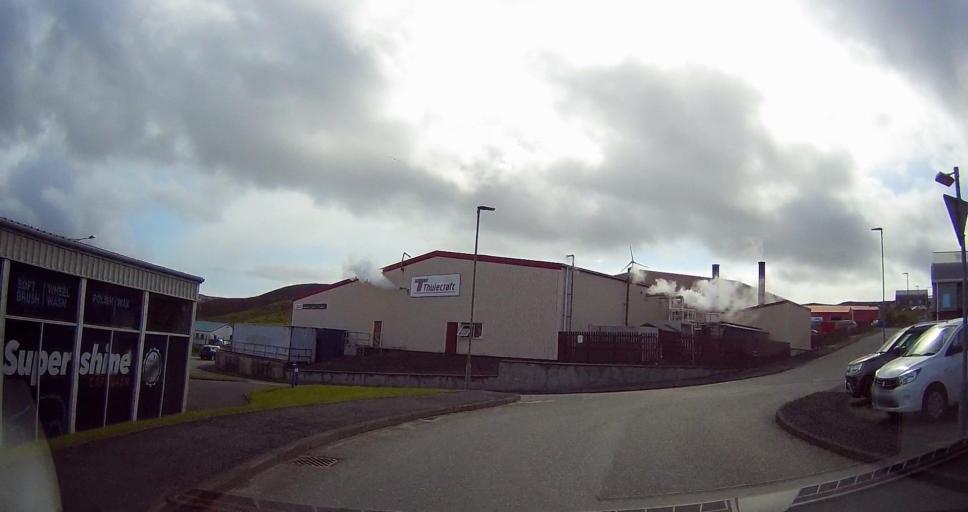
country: GB
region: Scotland
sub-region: Shetland Islands
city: Lerwick
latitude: 60.1697
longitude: -1.1680
